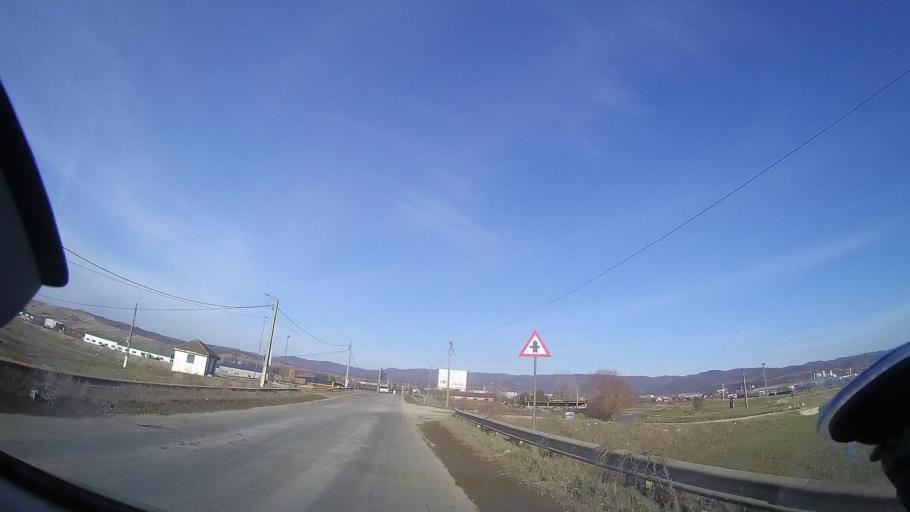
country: RO
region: Bihor
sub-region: Comuna Astileu
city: Astileu
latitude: 47.0471
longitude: 22.3912
